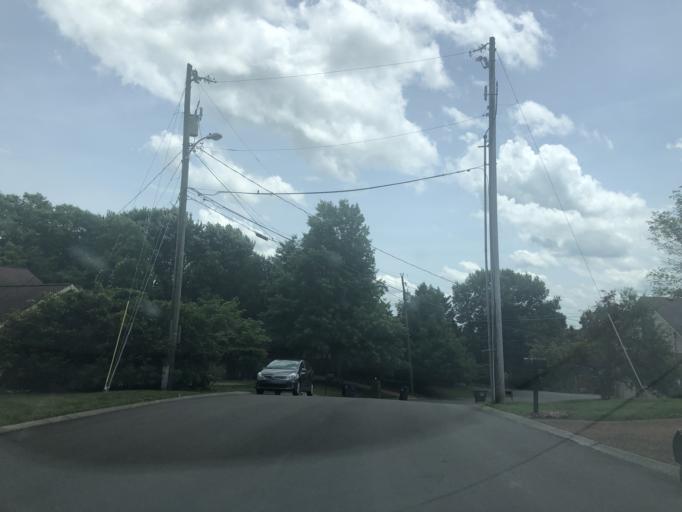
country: US
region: Tennessee
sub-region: Cheatham County
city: Pegram
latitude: 36.0521
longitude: -86.9571
